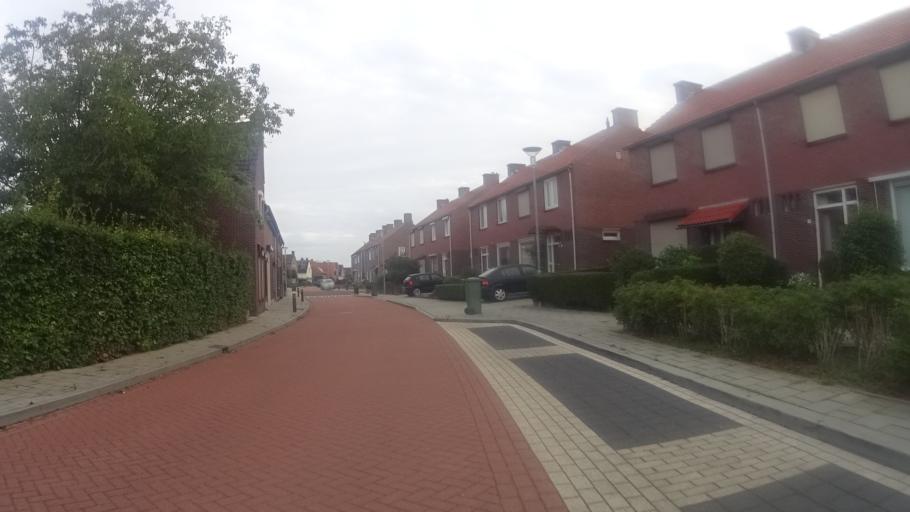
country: NL
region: Limburg
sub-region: Gemeente Venlo
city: Venlo
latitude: 51.4078
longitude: 6.1647
